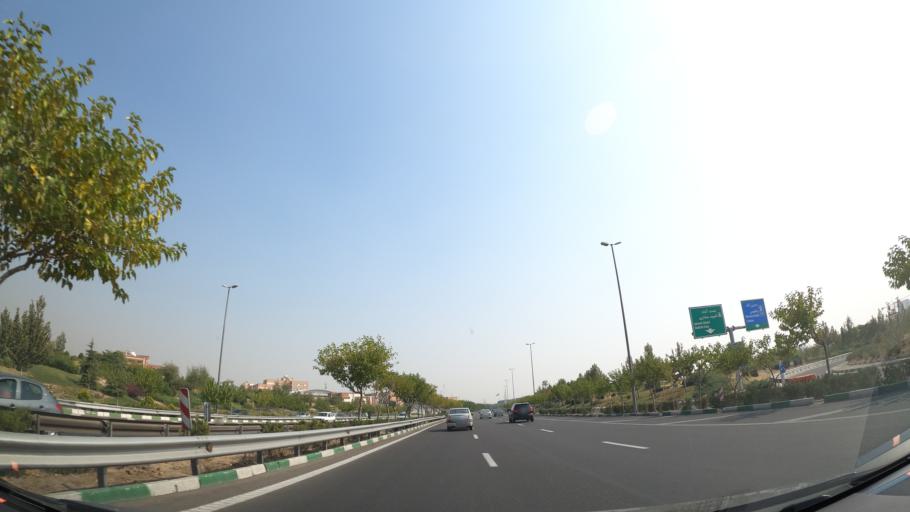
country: IR
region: Tehran
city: Shahr-e Qods
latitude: 35.7596
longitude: 51.2560
